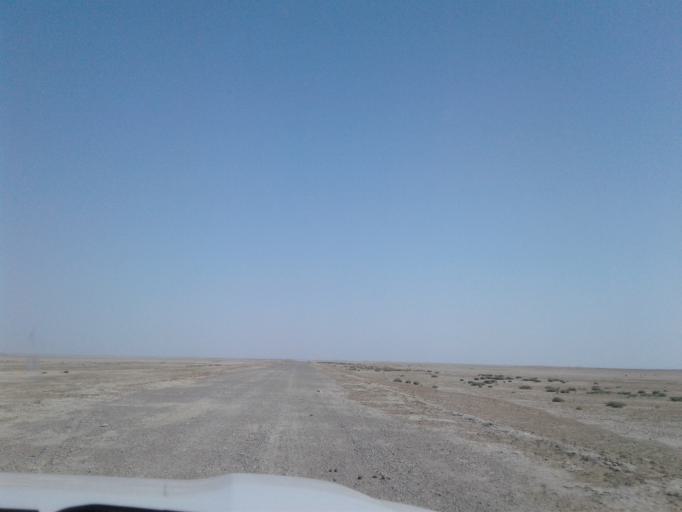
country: TM
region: Balkan
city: Gumdag
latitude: 38.3354
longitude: 54.5654
